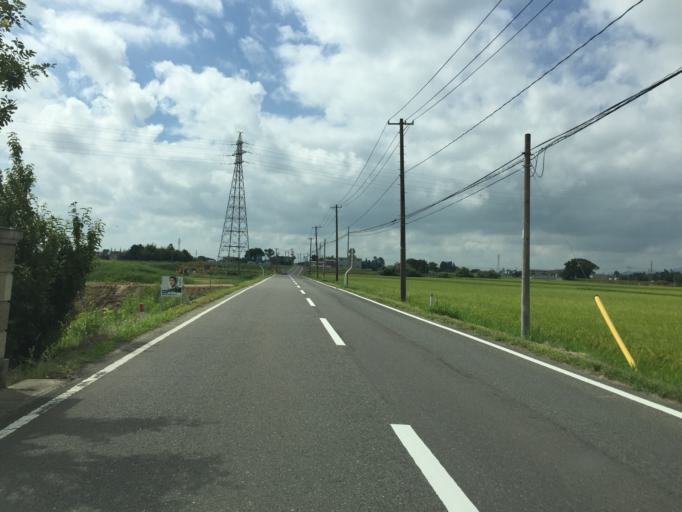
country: JP
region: Fukushima
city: Motomiya
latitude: 37.4668
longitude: 140.3405
